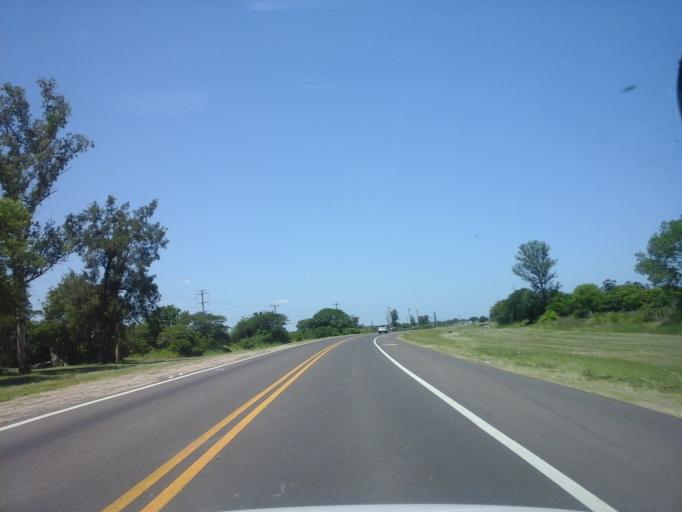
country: AR
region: Corrientes
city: Corrientes
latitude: -27.4295
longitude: -58.7257
